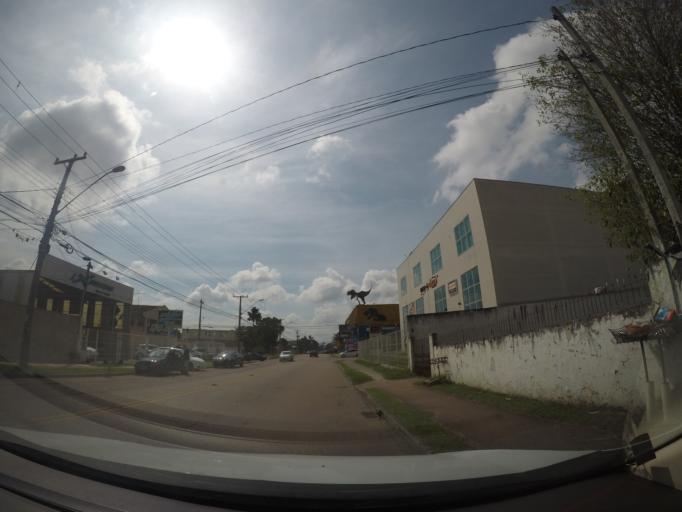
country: BR
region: Parana
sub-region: Curitiba
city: Curitiba
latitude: -25.4812
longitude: -49.2689
